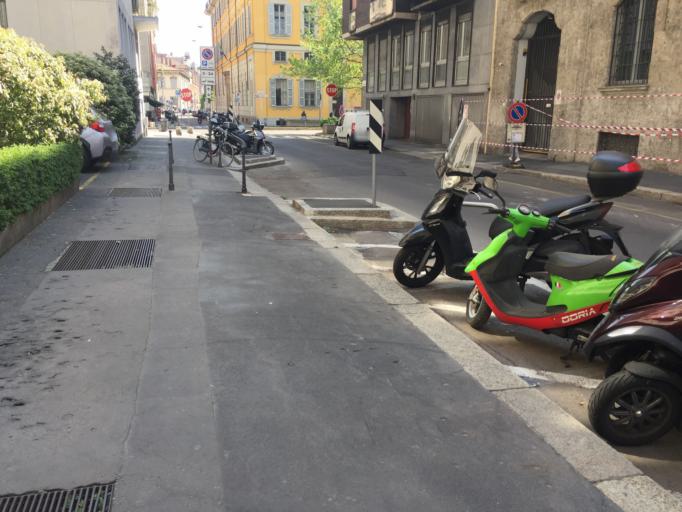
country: IT
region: Lombardy
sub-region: Citta metropolitana di Milano
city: Milano
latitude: 45.4666
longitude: 9.2024
